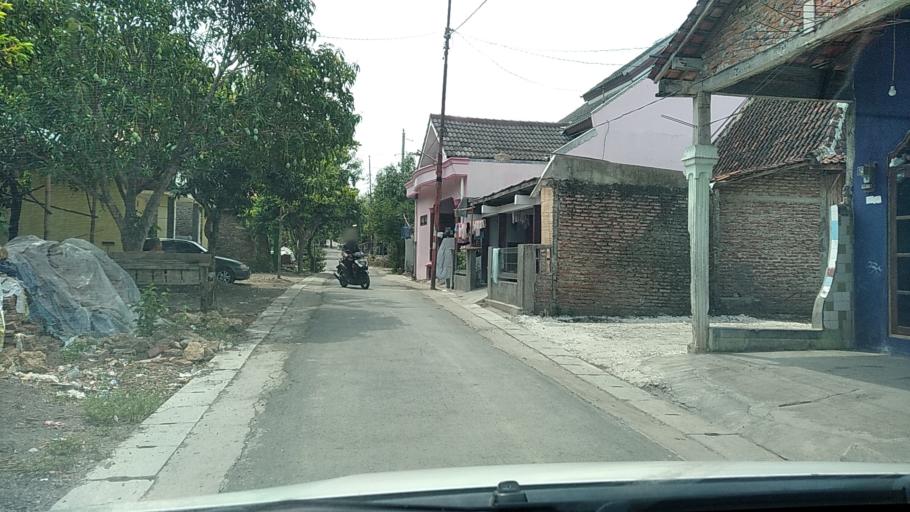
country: ID
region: Central Java
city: Mranggen
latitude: -7.0622
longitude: 110.4788
